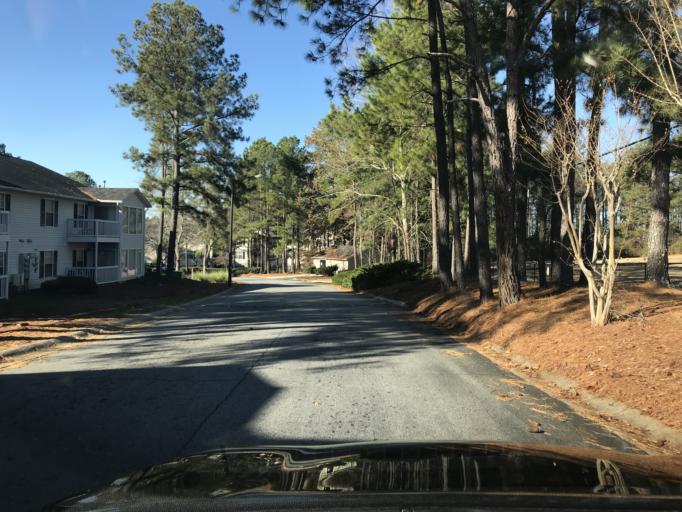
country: US
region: Georgia
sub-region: Clayton County
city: Riverdale
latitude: 33.5659
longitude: -84.3753
